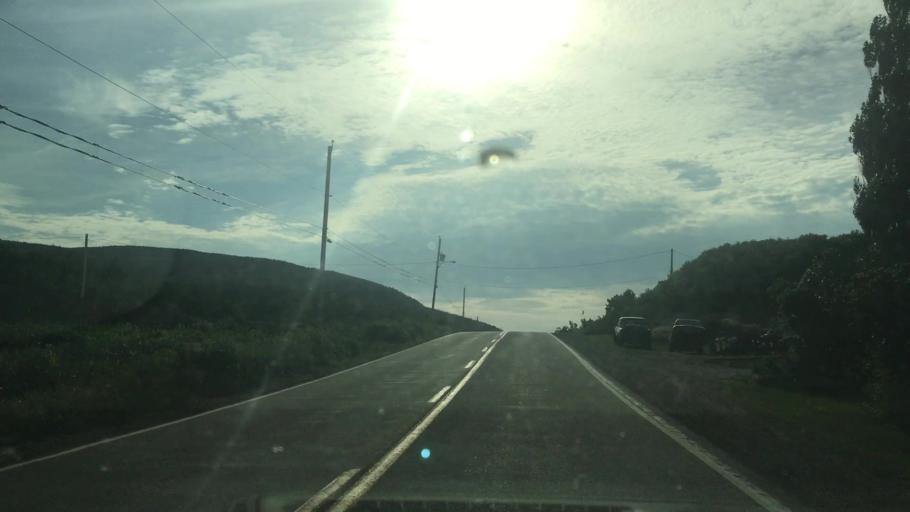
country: CA
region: Nova Scotia
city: Sydney Mines
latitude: 46.8244
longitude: -60.8183
